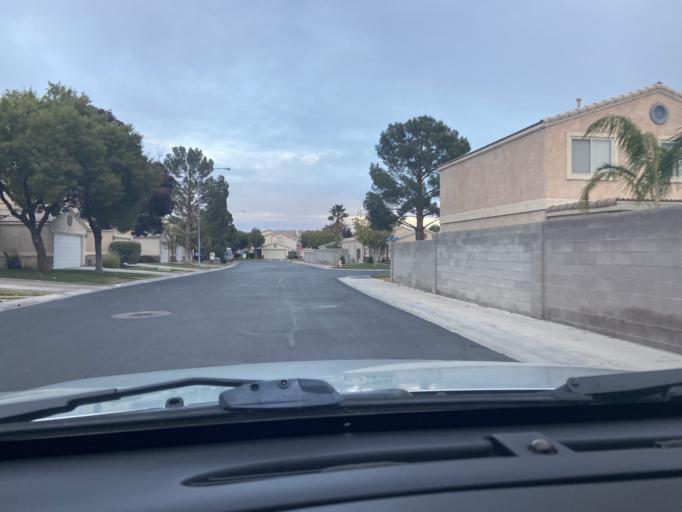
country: US
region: Nevada
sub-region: Clark County
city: Las Vegas
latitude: 36.2207
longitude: -115.1871
